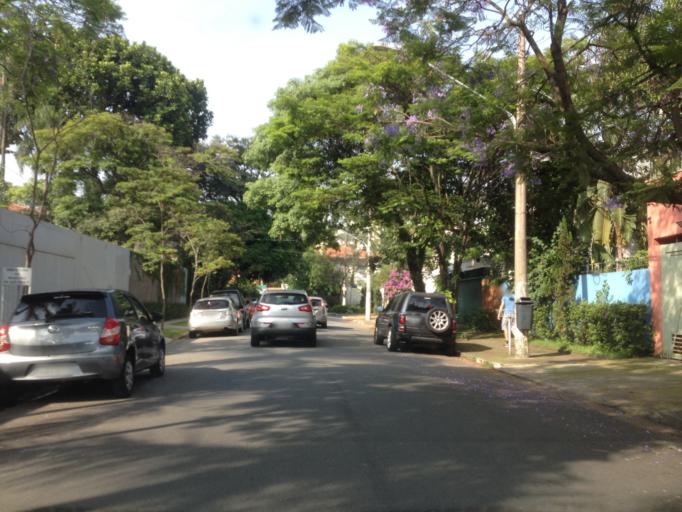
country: BR
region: Sao Paulo
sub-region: Sao Paulo
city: Sao Paulo
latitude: -23.5775
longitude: -46.6676
